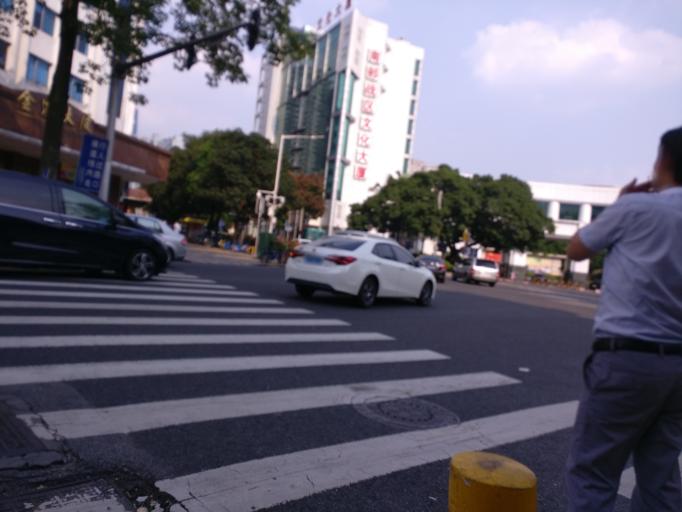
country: CN
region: Guangdong
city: Guangzhou
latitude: 23.1231
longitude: 113.2968
